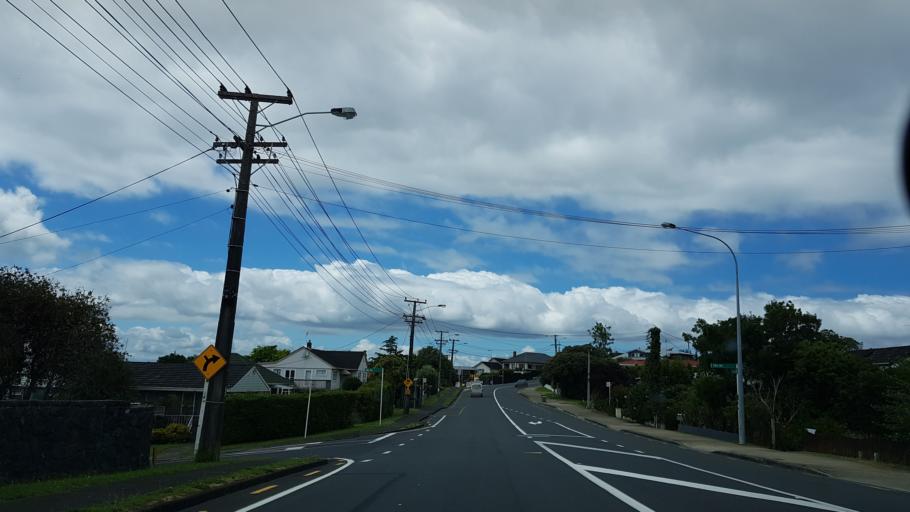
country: NZ
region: Auckland
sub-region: Auckland
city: North Shore
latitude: -36.7712
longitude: 174.7498
